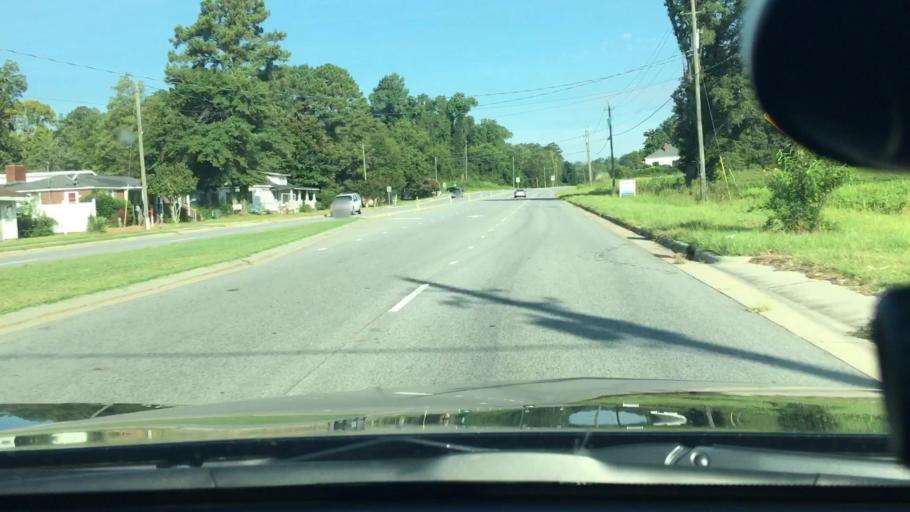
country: US
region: North Carolina
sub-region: Pitt County
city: Greenville
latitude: 35.6201
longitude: -77.4153
